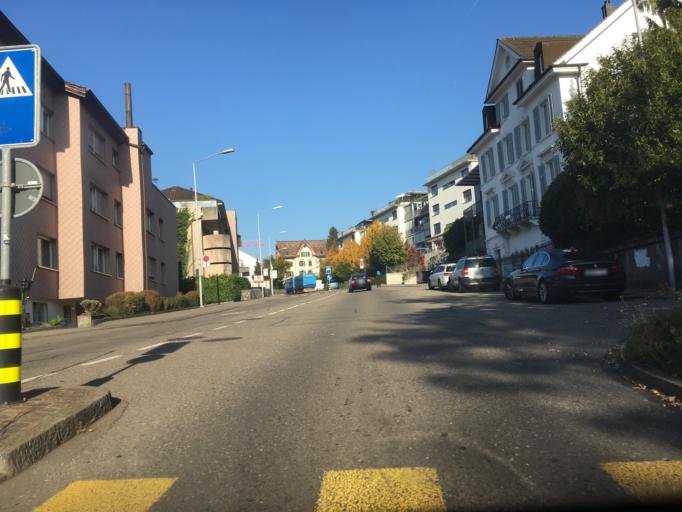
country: CH
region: Zurich
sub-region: Bezirk Zuerich
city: Zuerich (Kreis 10) / Hoengg
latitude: 47.3977
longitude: 8.5024
